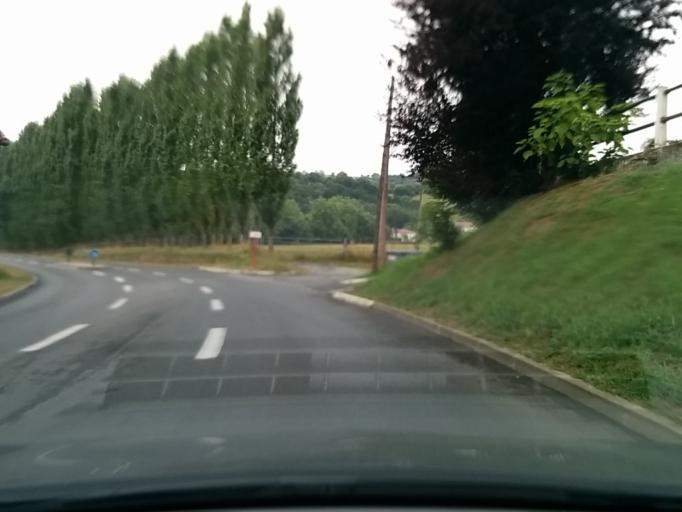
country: FR
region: Aquitaine
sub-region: Departement des Pyrenees-Atlantiques
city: Saint-Pee-sur-Nivelle
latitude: 43.3392
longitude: -1.5504
